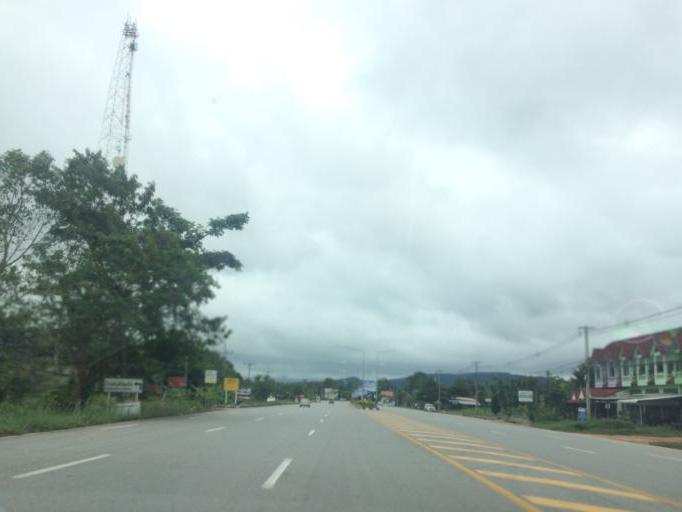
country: TH
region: Chiang Rai
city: Mae Lao
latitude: 19.7469
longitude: 99.7197
